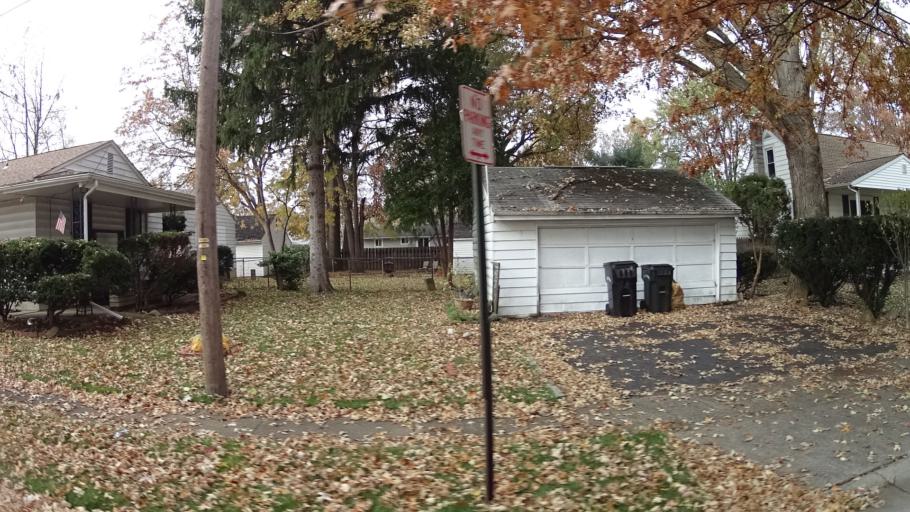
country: US
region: Ohio
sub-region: Lorain County
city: Elyria
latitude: 41.3637
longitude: -82.0805
